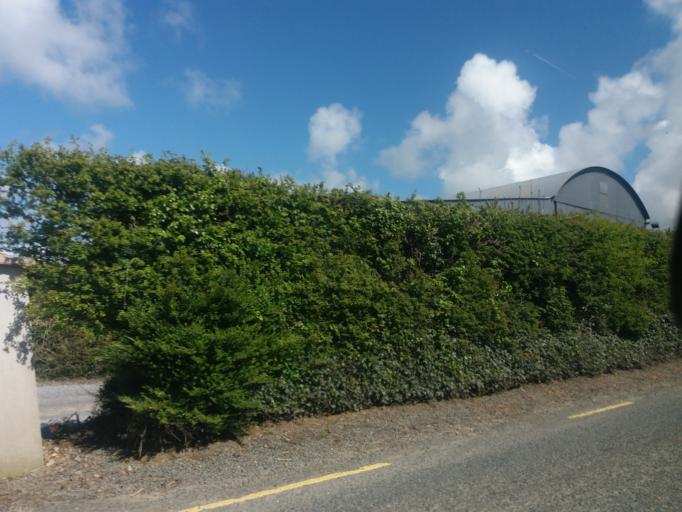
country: IE
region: Leinster
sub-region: Loch Garman
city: New Ross
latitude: 52.2561
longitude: -6.8168
